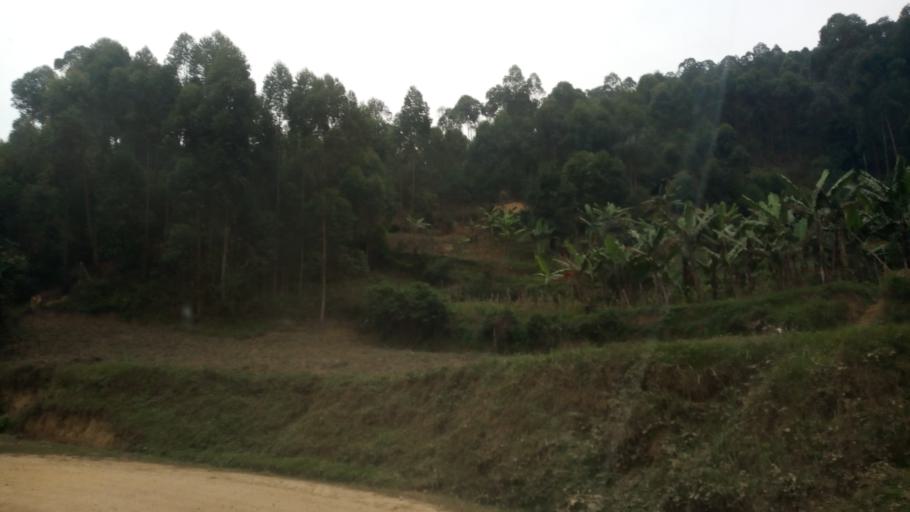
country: UG
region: Western Region
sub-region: Kanungu District
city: Kanungu
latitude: -1.1023
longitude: 29.8569
